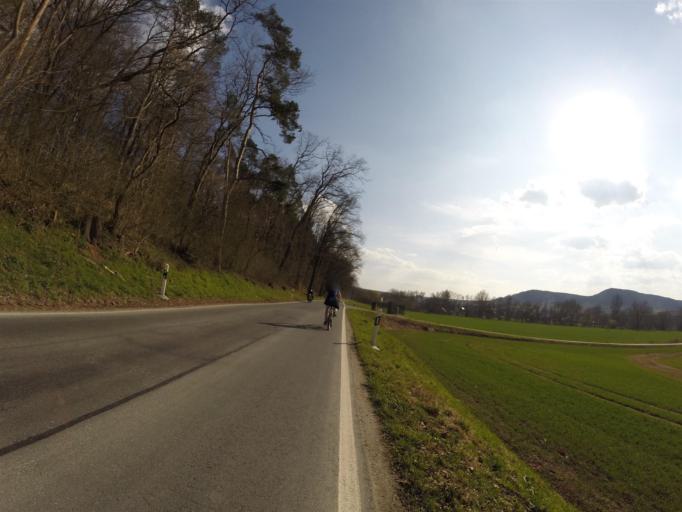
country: DE
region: Thuringia
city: Sulza
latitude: 50.8730
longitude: 11.6075
